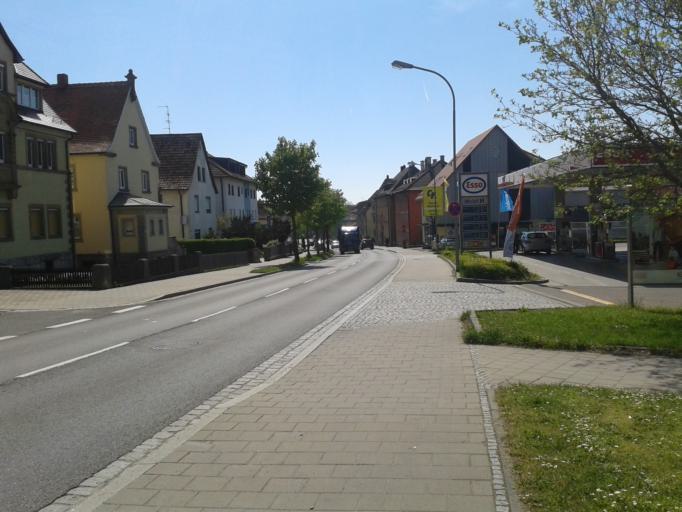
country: DE
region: Bavaria
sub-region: Regierungsbezirk Mittelfranken
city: Rothenburg ob der Tauber
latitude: 49.3791
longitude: 10.1872
